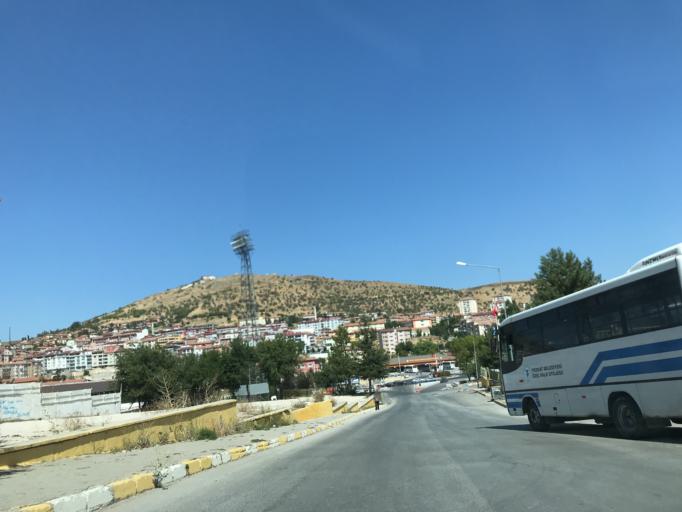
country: TR
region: Yozgat
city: Yozgat
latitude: 39.8210
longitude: 34.8178
